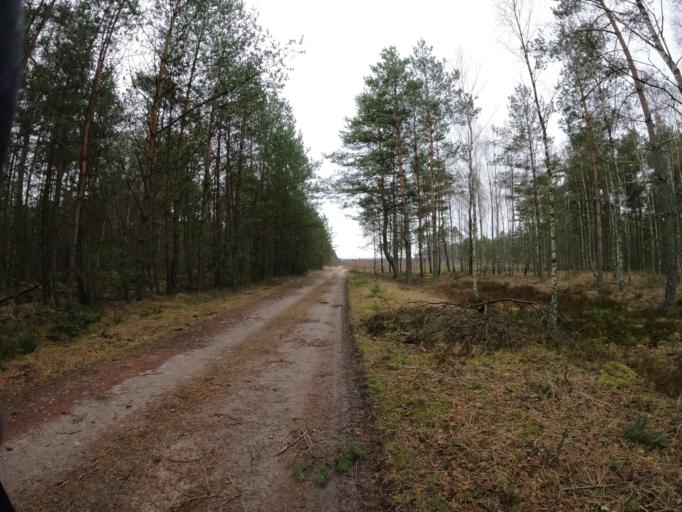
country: PL
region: Greater Poland Voivodeship
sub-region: Powiat zlotowski
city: Sypniewo
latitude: 53.5139
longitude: 16.5628
